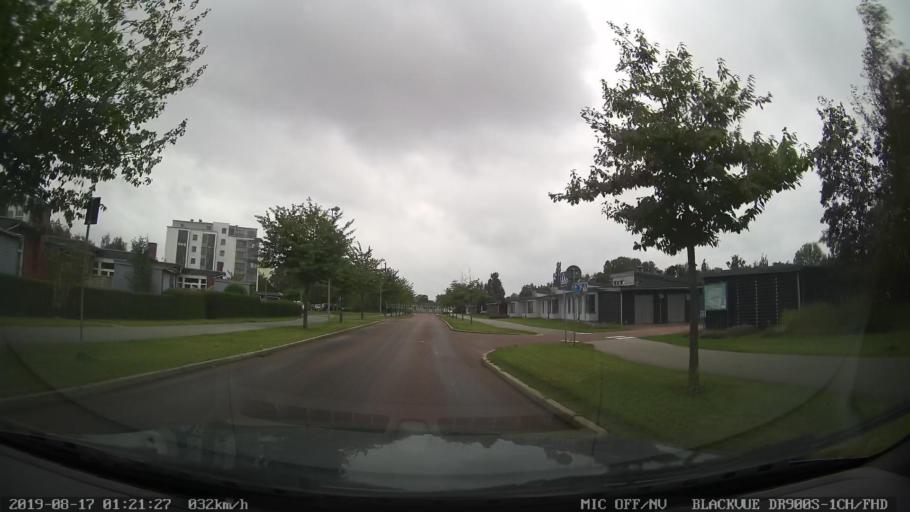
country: SE
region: Skane
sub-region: Landskrona
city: Landskrona
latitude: 55.8932
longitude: 12.8251
